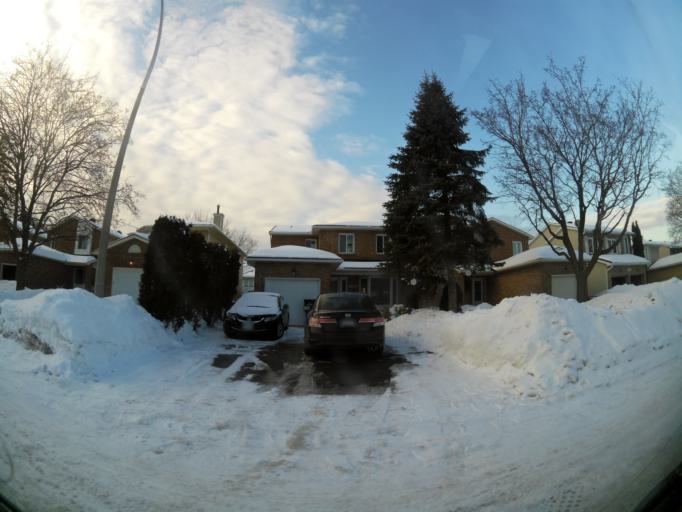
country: CA
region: Ontario
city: Ottawa
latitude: 45.4524
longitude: -75.5431
